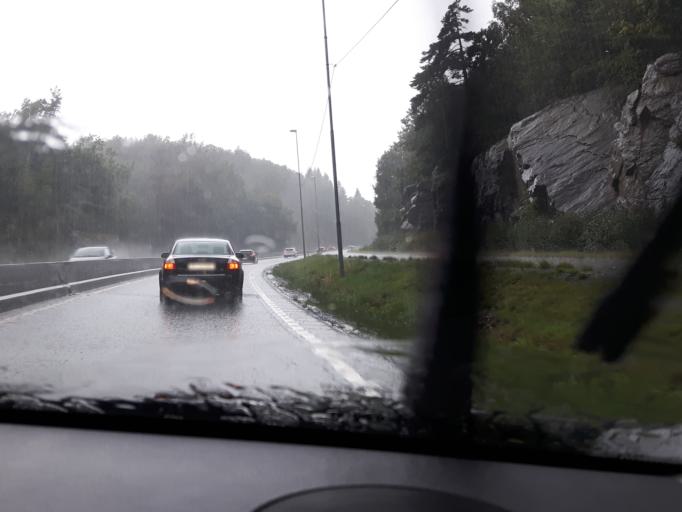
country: NO
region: Vest-Agder
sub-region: Kristiansand
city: Strai
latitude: 58.1429
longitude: 7.9050
